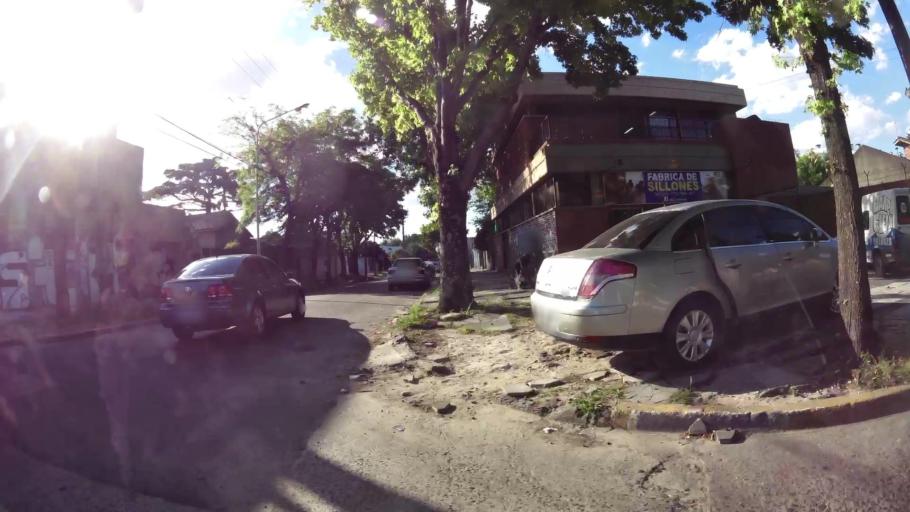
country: AR
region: Buenos Aires
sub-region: Partido de General San Martin
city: General San Martin
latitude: -34.5373
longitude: -58.5622
